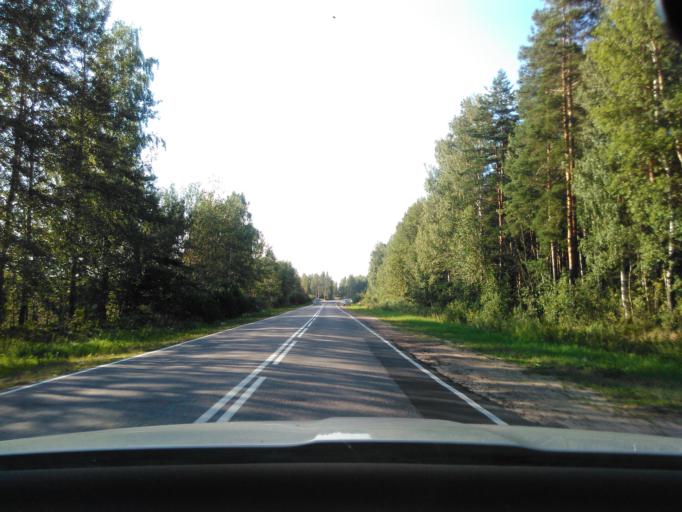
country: RU
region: Tverskaya
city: Zavidovo
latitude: 56.5932
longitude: 36.5412
